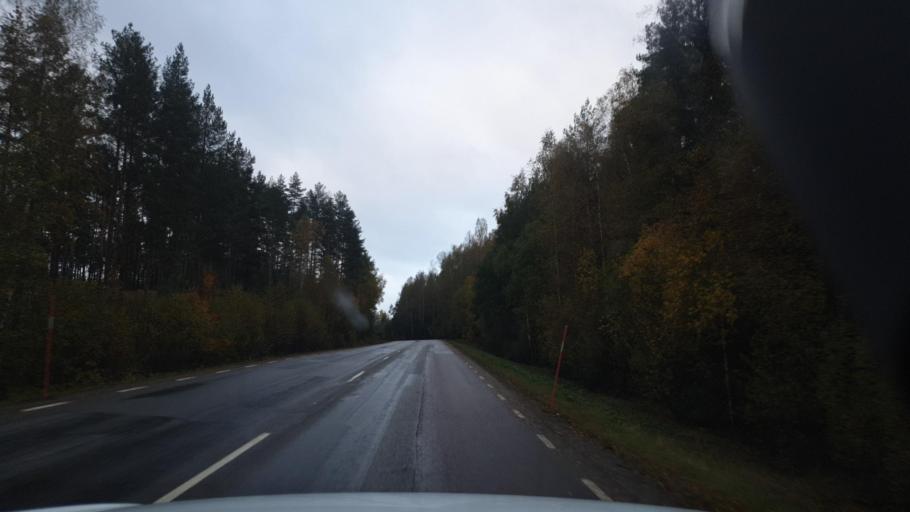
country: SE
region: Vaermland
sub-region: Arvika Kommun
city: Arvika
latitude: 59.6722
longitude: 12.6276
